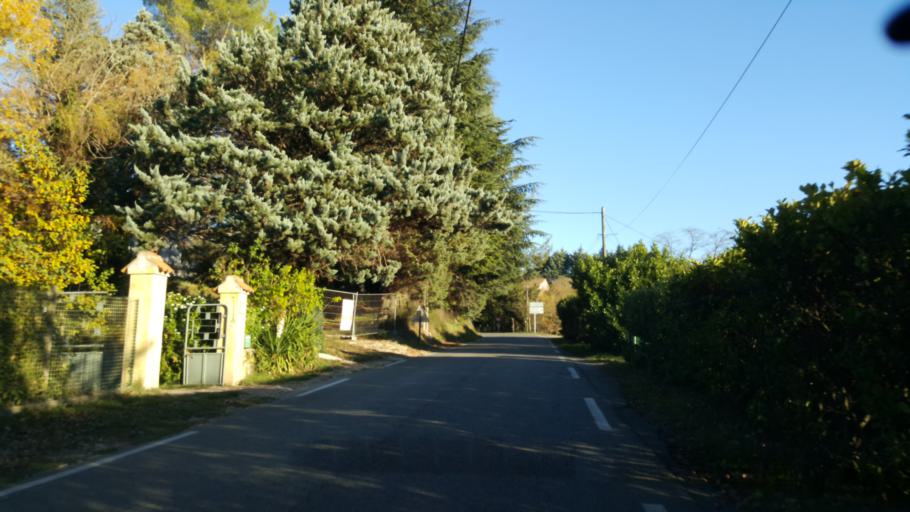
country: FR
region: Provence-Alpes-Cote d'Azur
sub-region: Departement du Var
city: Barjols
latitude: 43.5978
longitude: 5.9560
